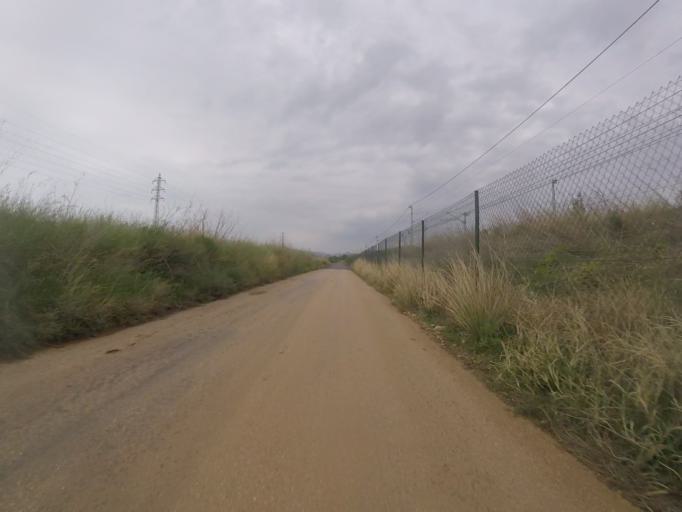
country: ES
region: Valencia
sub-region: Provincia de Castello
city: Torreblanca
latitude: 40.2158
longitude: 0.2034
